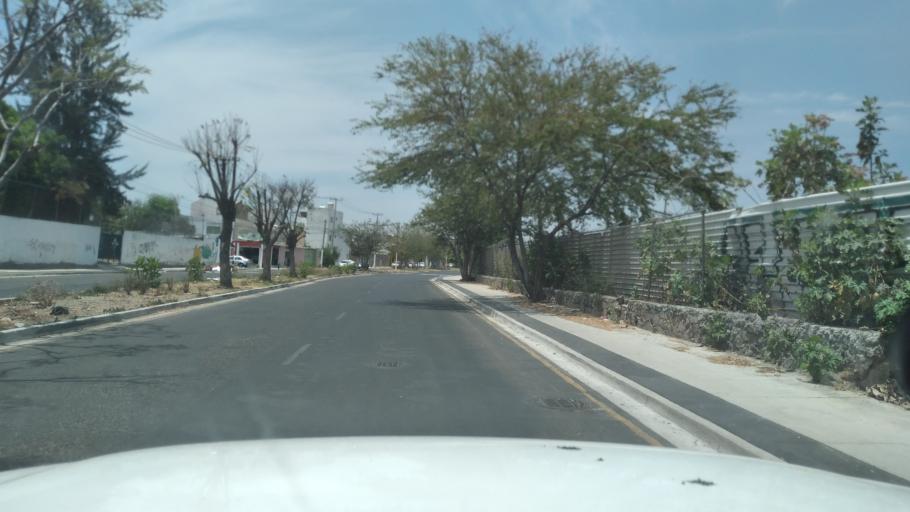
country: MX
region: Jalisco
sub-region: Zapopan
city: Zapopan
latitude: 20.7310
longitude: -103.3740
